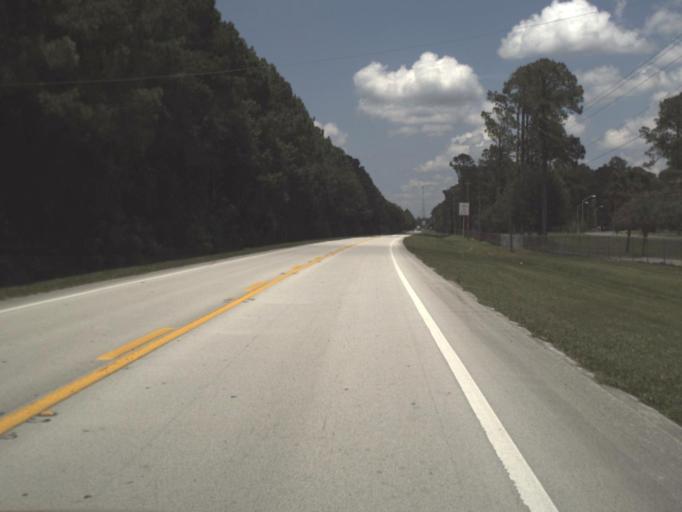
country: US
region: Florida
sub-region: Baker County
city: Macclenny
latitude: 30.2373
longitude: -82.1383
